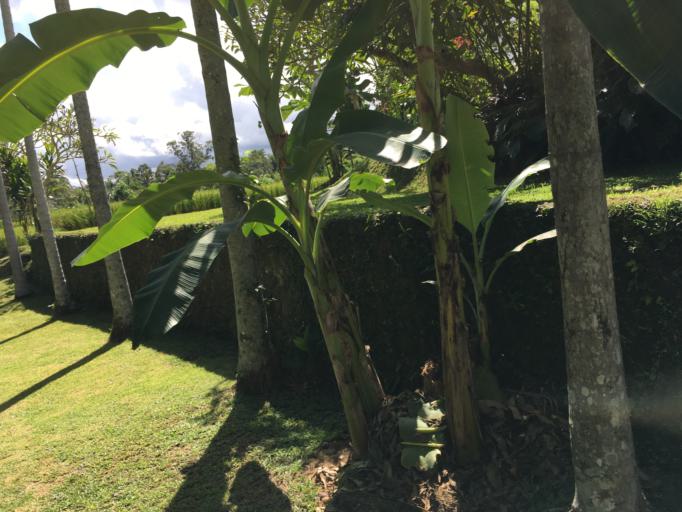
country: ID
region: Bali
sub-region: Kabupaten Gianyar
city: Ubud
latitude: -8.4960
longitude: 115.2519
